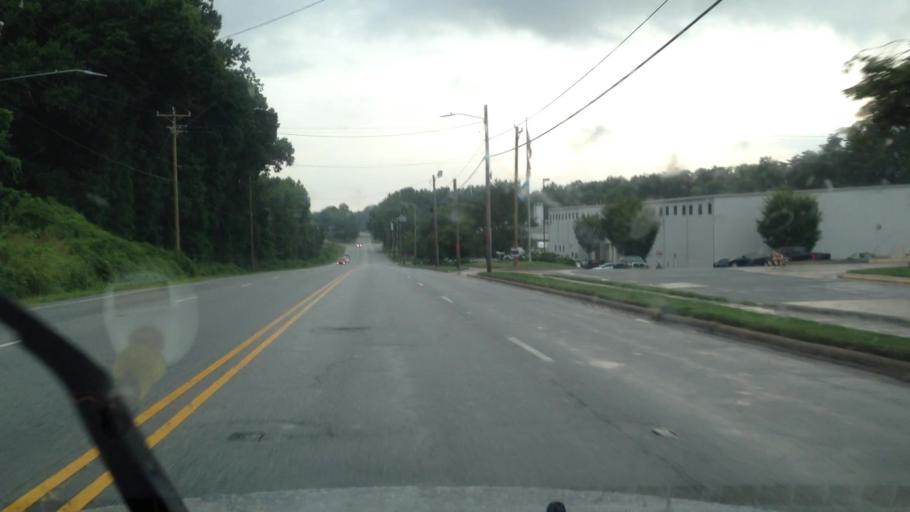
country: US
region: North Carolina
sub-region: Guilford County
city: Greensboro
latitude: 36.0565
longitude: -79.8458
